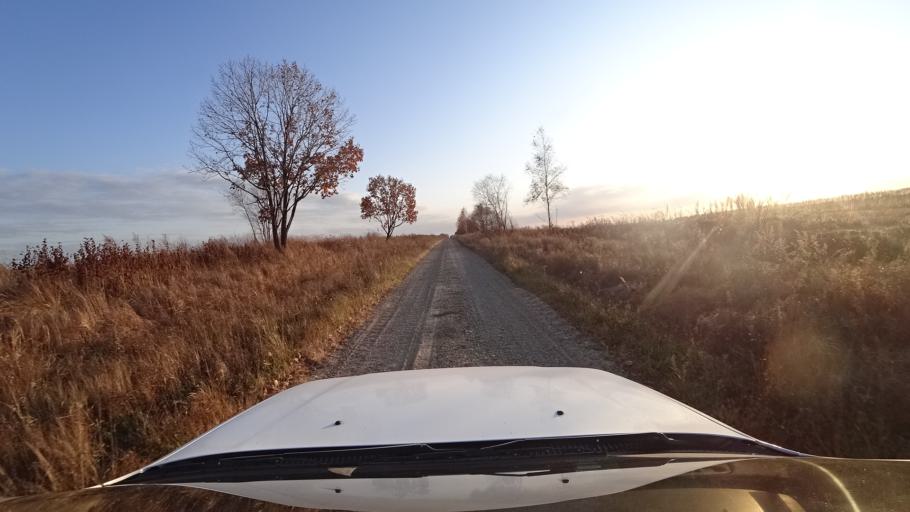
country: RU
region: Primorskiy
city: Lazo
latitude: 45.8131
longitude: 133.6094
